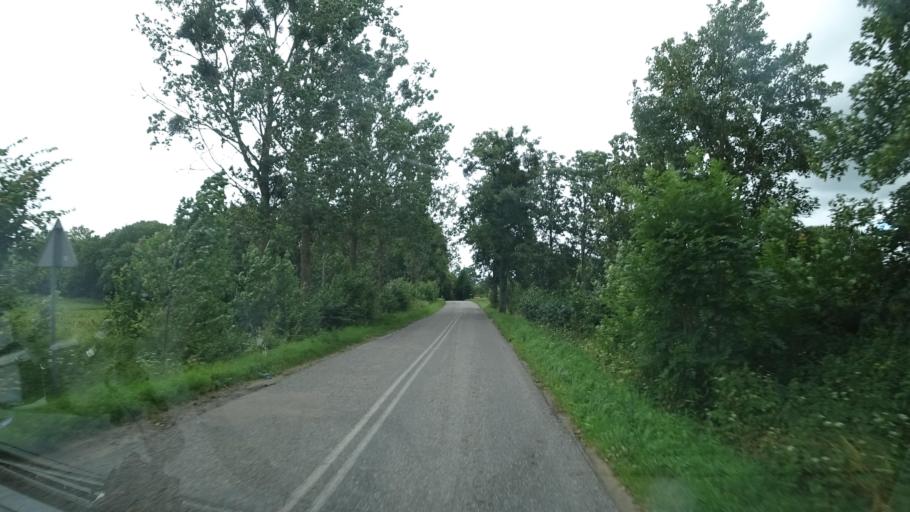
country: PL
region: Warmian-Masurian Voivodeship
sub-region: Powiat olecki
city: Kowale Oleckie
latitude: 54.2892
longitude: 22.5085
